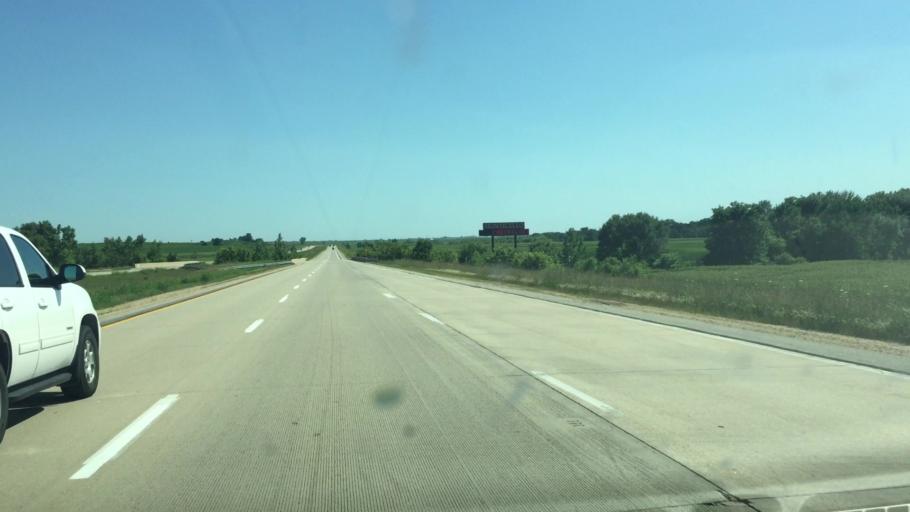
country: US
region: Iowa
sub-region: Jones County
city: Monticello
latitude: 42.2254
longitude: -91.1721
